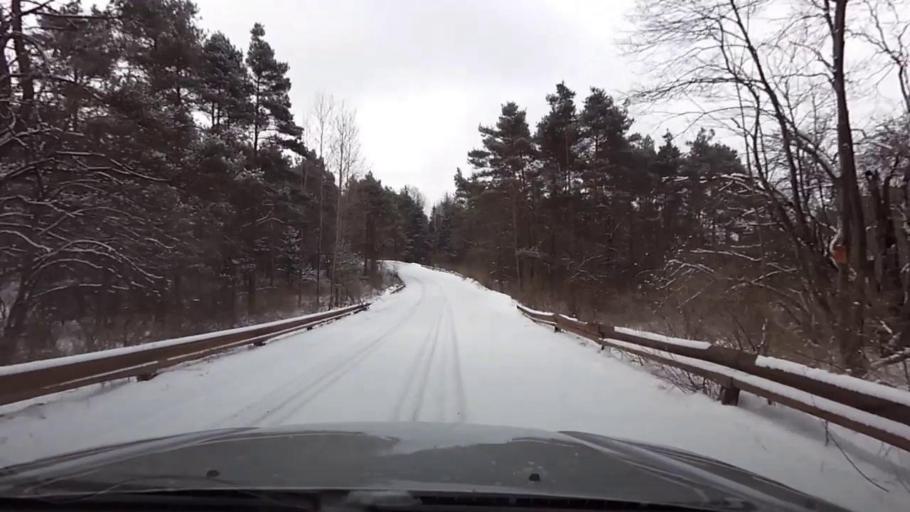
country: US
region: New York
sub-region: Cattaraugus County
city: Franklinville
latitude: 42.3389
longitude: -78.3687
